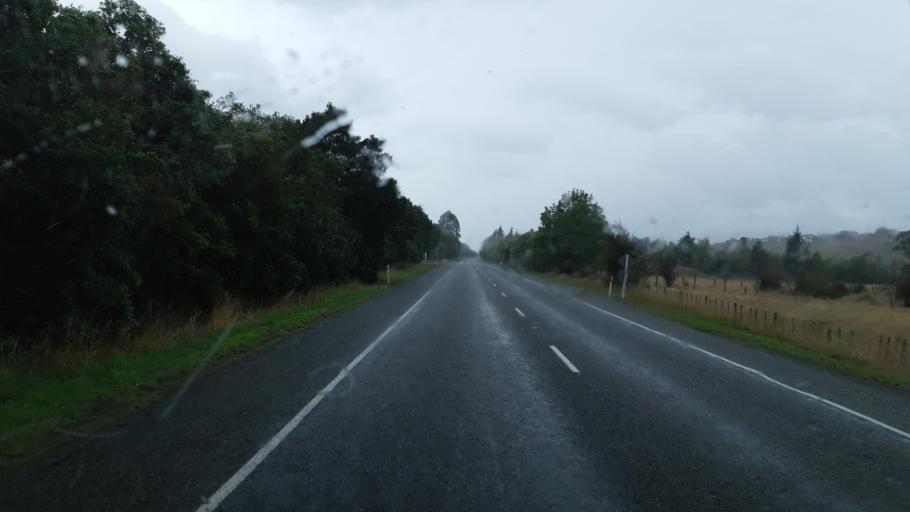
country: NZ
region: Tasman
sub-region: Tasman District
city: Brightwater
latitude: -41.3804
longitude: 173.0895
